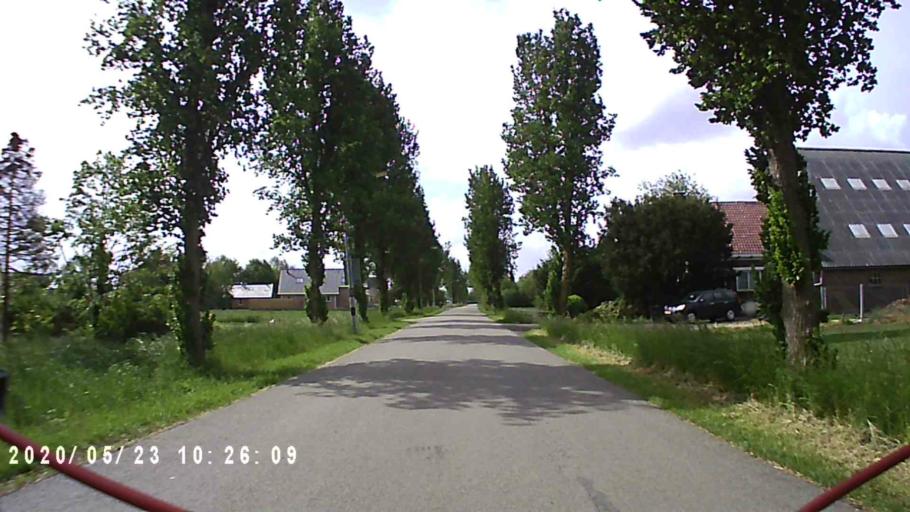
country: NL
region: Groningen
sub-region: Gemeente Appingedam
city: Appingedam
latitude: 53.3046
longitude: 6.8523
